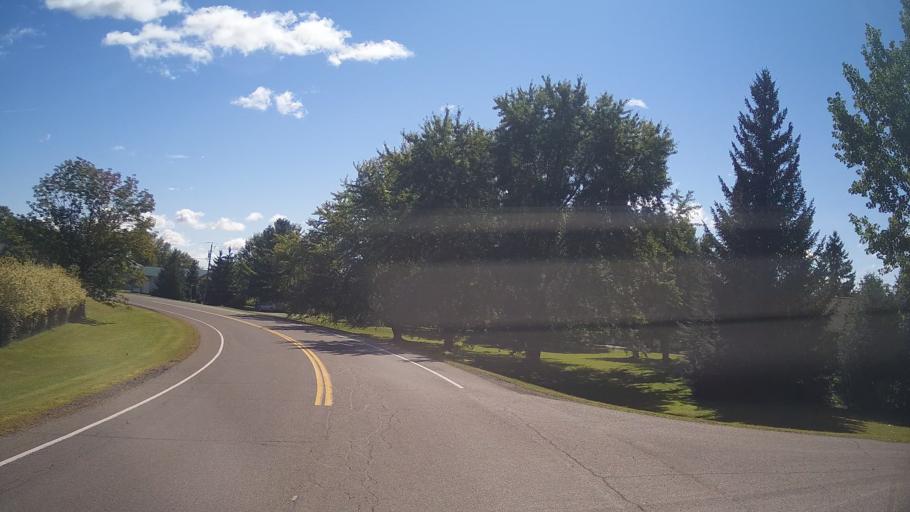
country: US
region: New York
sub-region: St. Lawrence County
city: Norfolk
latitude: 44.9713
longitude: -75.2518
